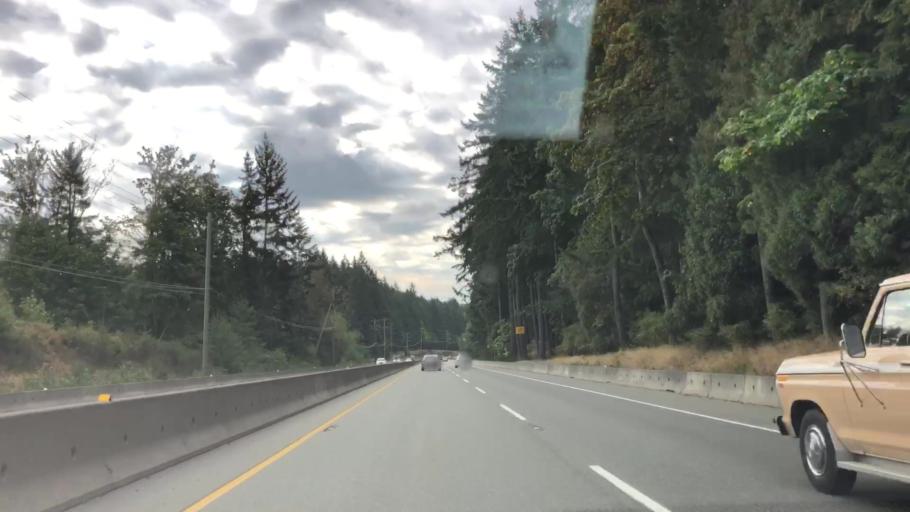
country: CA
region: British Columbia
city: North Cowichan
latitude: 48.8907
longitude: -123.7083
